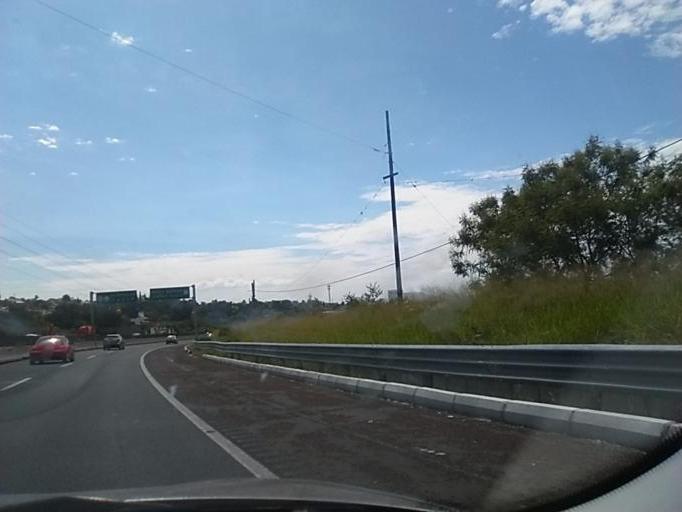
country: MX
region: Morelos
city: Temixco
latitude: 18.8657
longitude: -99.2220
